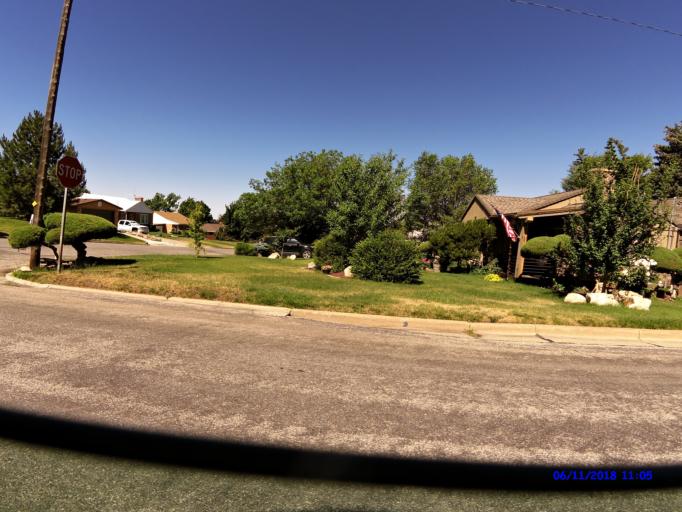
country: US
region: Utah
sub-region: Weber County
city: Ogden
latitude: 41.2181
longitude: -111.9318
